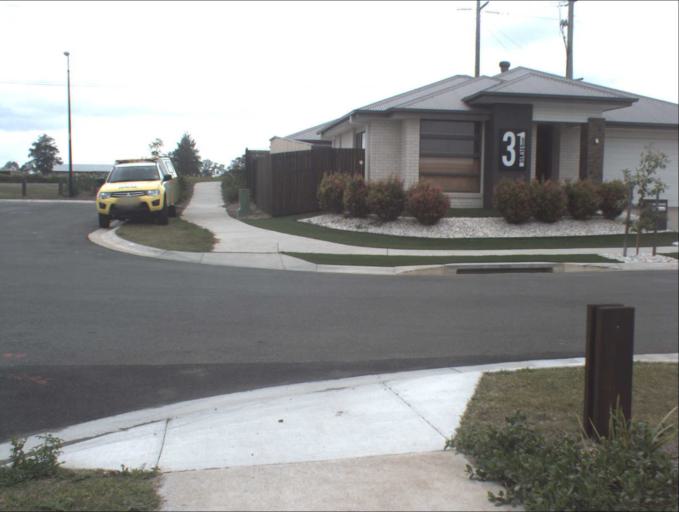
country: AU
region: Queensland
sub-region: Logan
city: Waterford West
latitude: -27.7094
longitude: 153.1159
